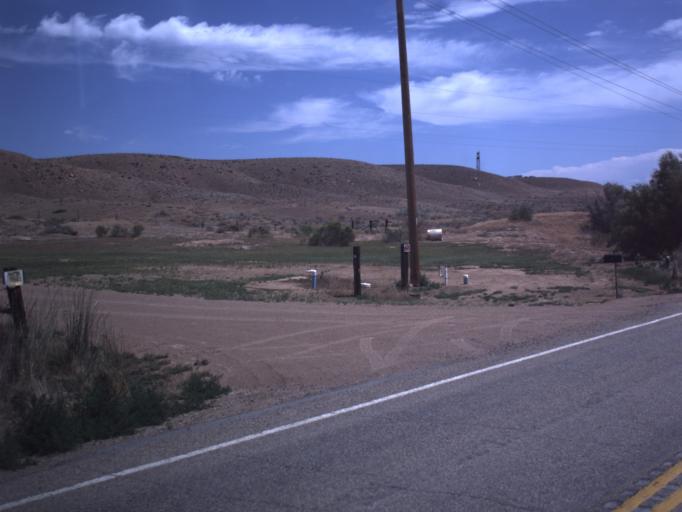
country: US
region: Utah
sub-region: Uintah County
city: Naples
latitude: 40.2155
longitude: -109.6760
